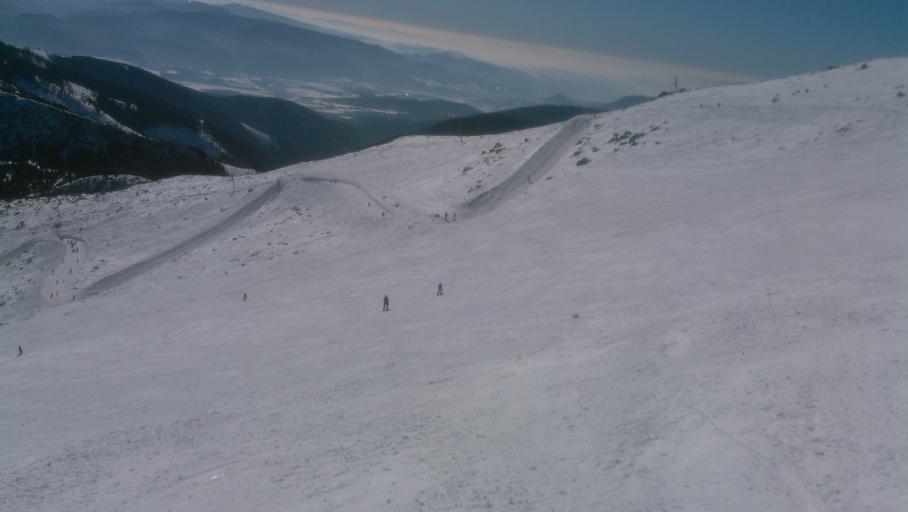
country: SK
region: Zilinsky
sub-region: Okres Liptovsky Mikulas
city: Liptovsky Mikulas
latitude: 48.9400
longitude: 19.5807
